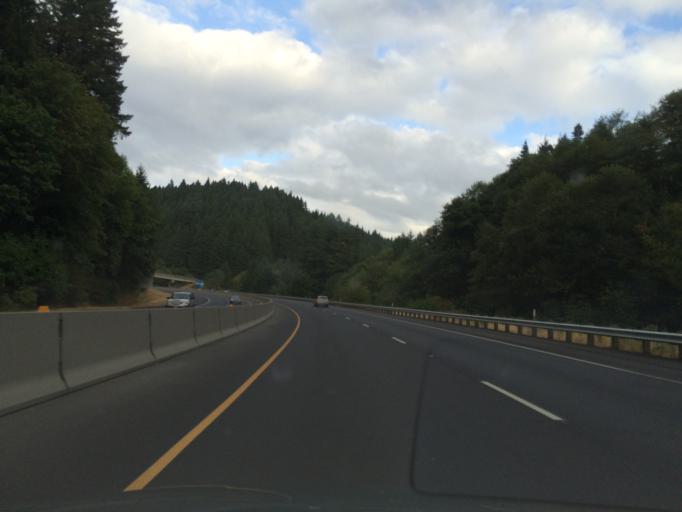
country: US
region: Oregon
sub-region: Lane County
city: Cottage Grove
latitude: 43.7517
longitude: -123.1492
